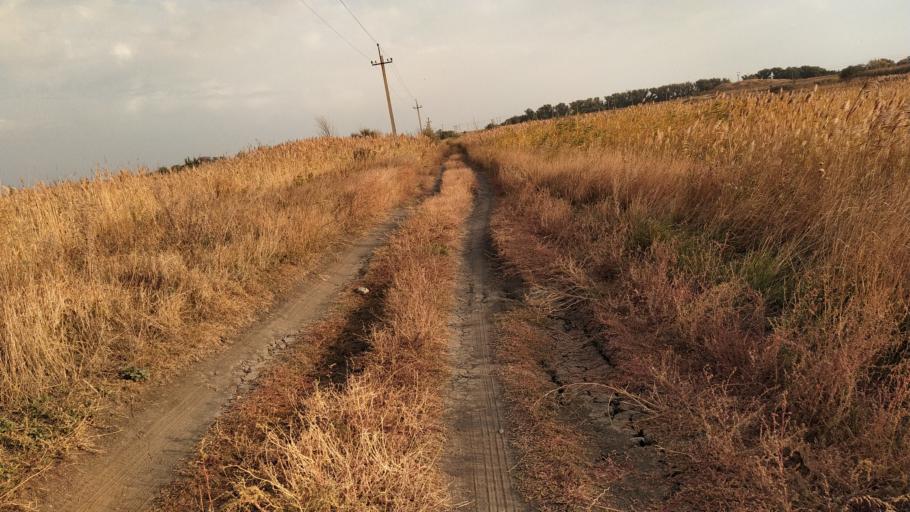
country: RU
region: Rostov
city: Kuleshovka
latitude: 47.1124
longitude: 39.6084
